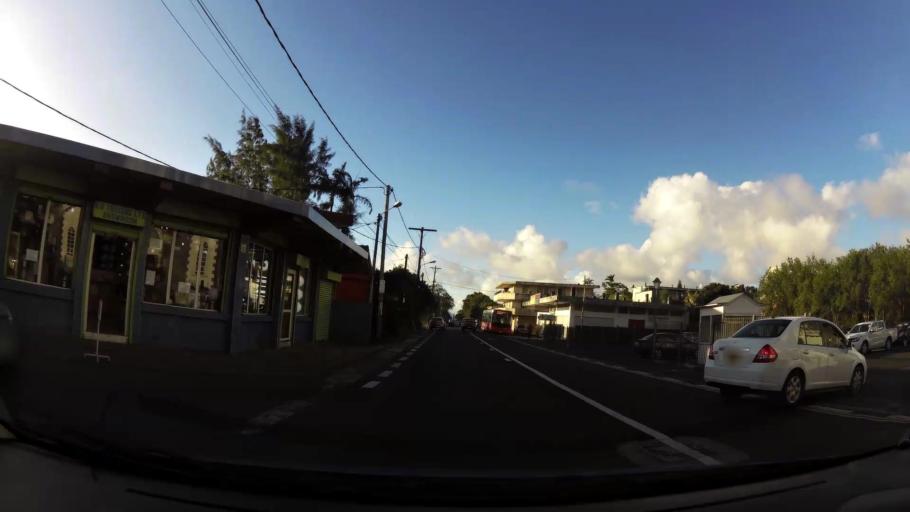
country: MU
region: Plaines Wilhems
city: Curepipe
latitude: -20.3113
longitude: 57.5242
